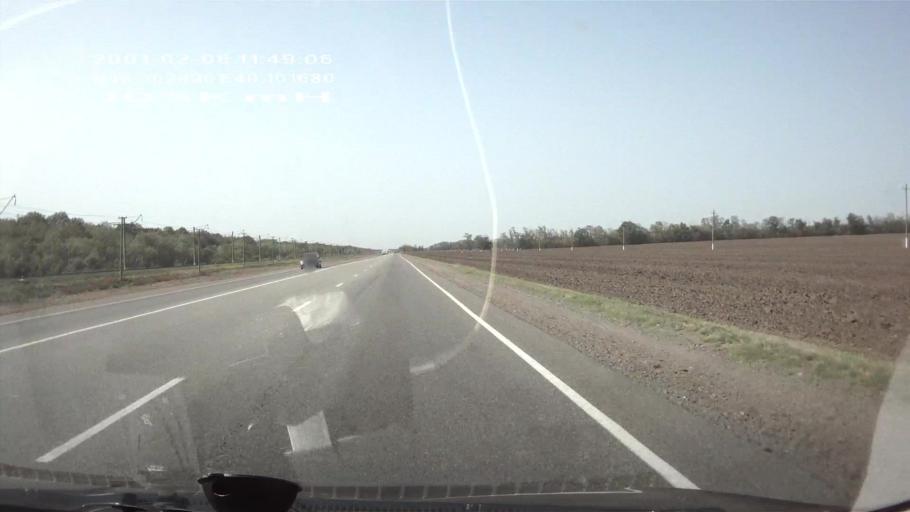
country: RU
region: Krasnodarskiy
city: Tbilisskaya
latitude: 45.3630
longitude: 40.1007
